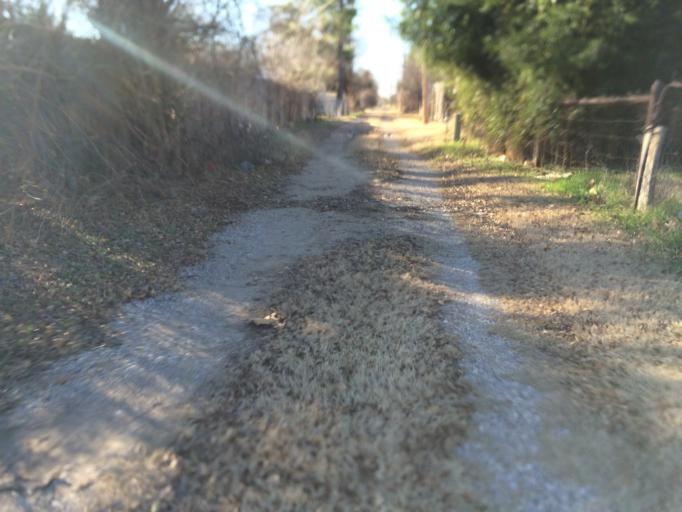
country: US
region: Oklahoma
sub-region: Cleveland County
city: Norman
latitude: 35.2320
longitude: -97.4463
